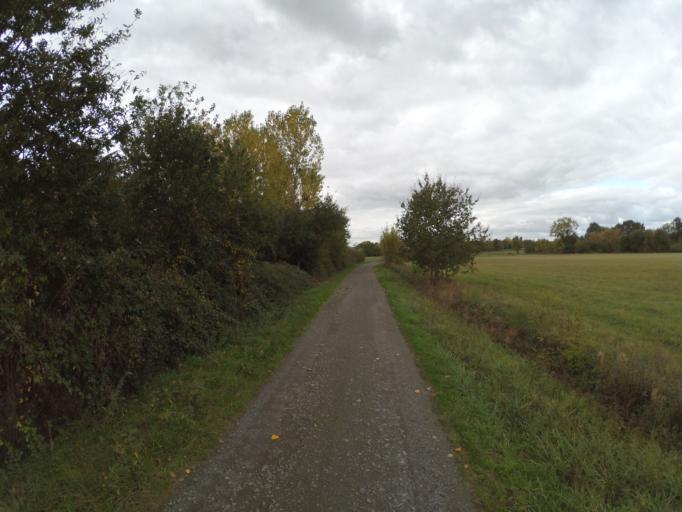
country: FR
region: Pays de la Loire
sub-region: Departement de la Loire-Atlantique
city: Saint-Lumine-de-Clisson
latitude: 47.0559
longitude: -1.3428
